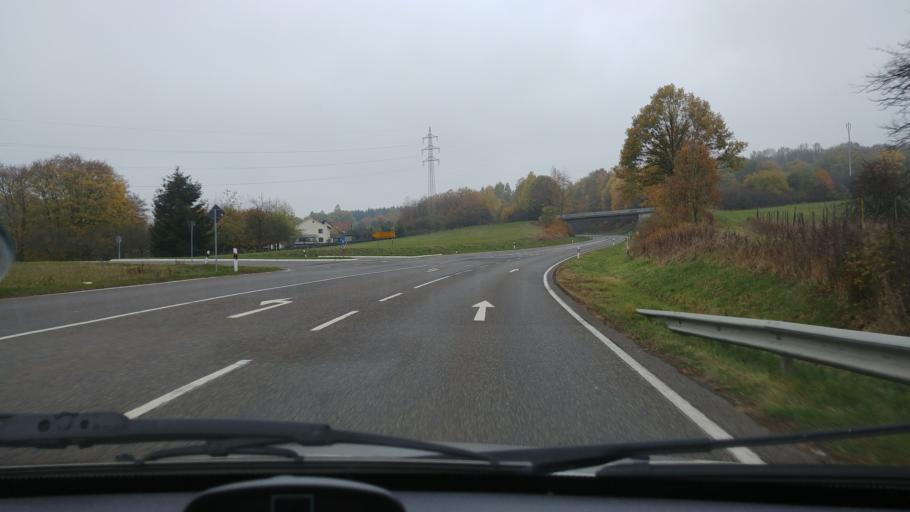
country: DE
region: Rheinland-Pfalz
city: Langenhahn
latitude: 50.5811
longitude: 7.9290
